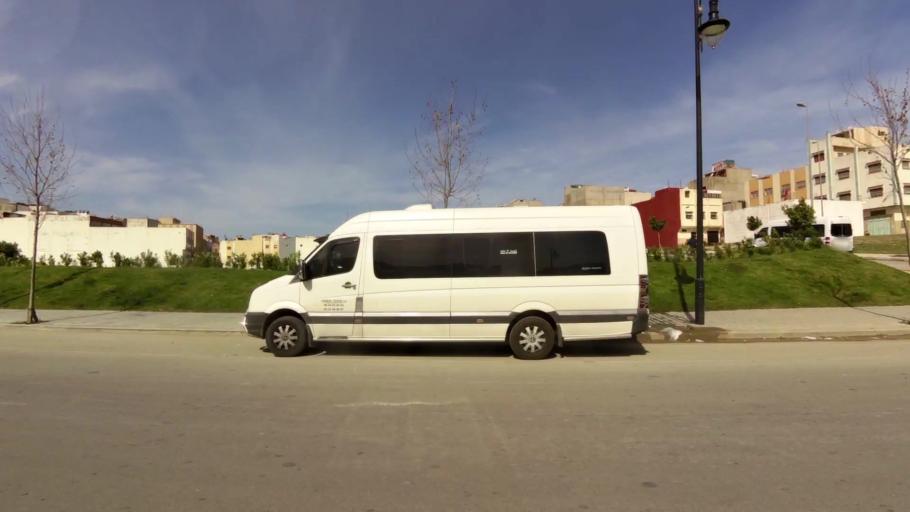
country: MA
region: Tanger-Tetouan
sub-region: Tanger-Assilah
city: Tangier
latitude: 35.7281
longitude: -5.8032
